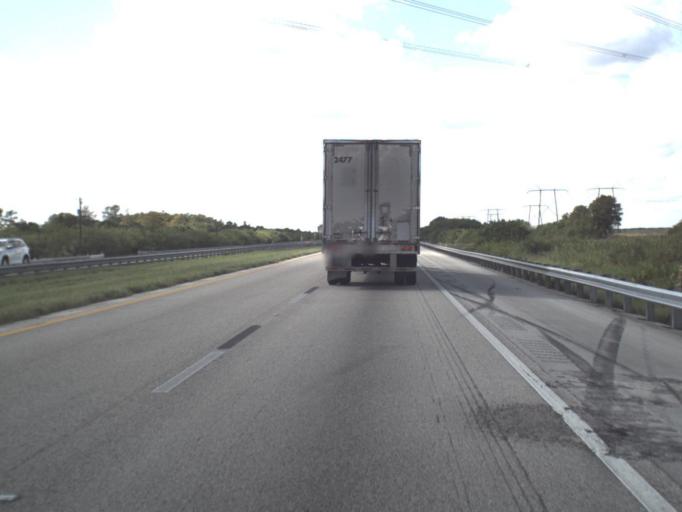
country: US
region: Florida
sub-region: Indian River County
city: West Vero Corridor
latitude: 27.5595
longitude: -80.6589
